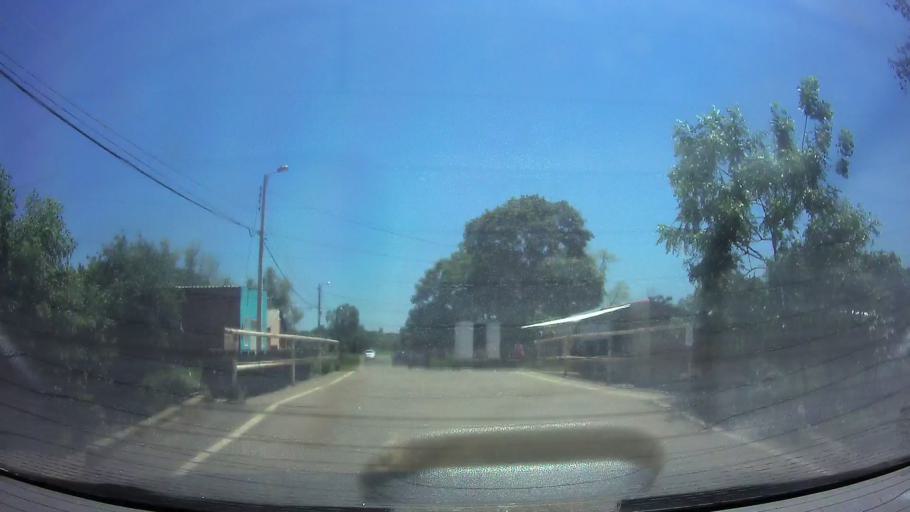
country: PY
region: Central
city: San Lorenzo
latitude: -25.3245
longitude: -57.4828
